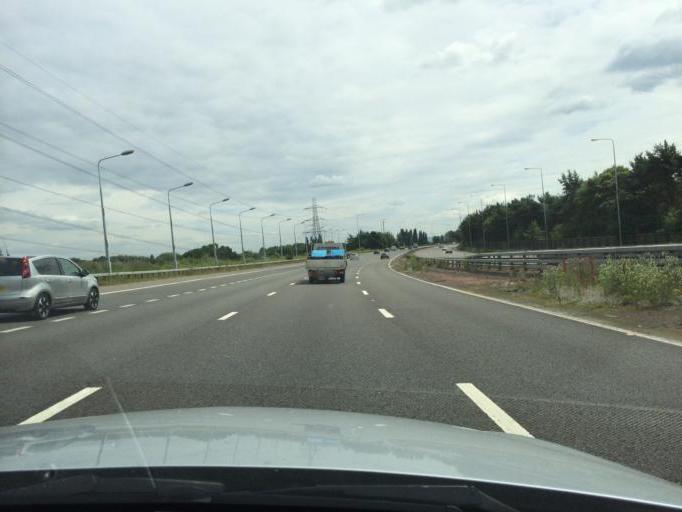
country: GB
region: England
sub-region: Manchester
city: Chorlton cum Hardy
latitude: 53.4134
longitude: -2.2590
